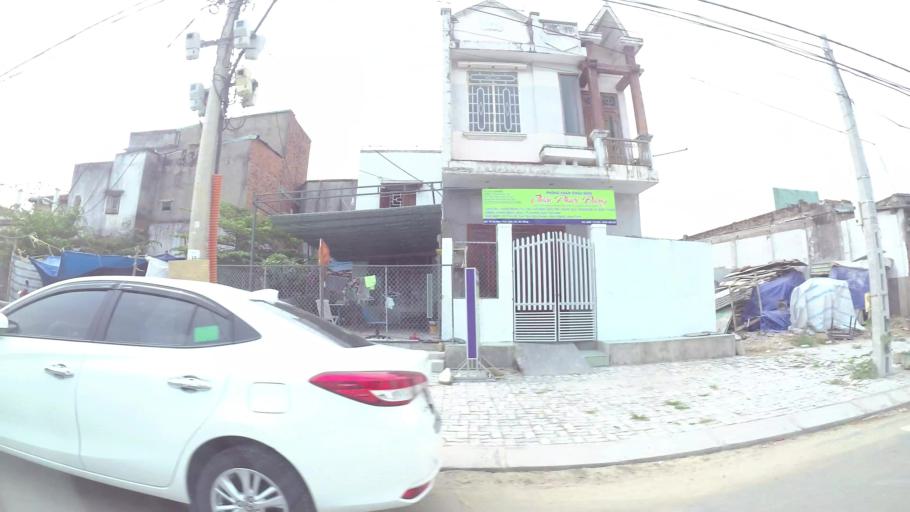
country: VN
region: Da Nang
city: Son Tra
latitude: 16.0883
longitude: 108.2439
